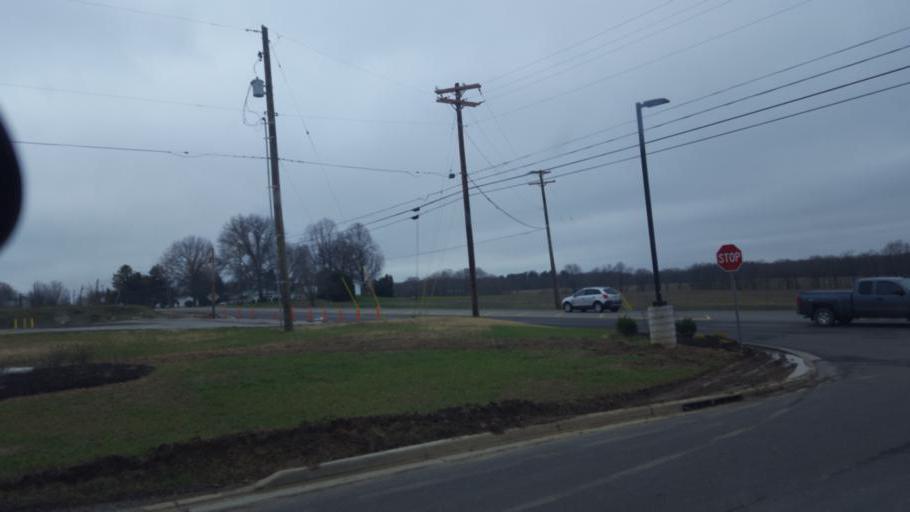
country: US
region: Ohio
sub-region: Ashland County
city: Ashland
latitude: 40.7830
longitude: -82.2619
